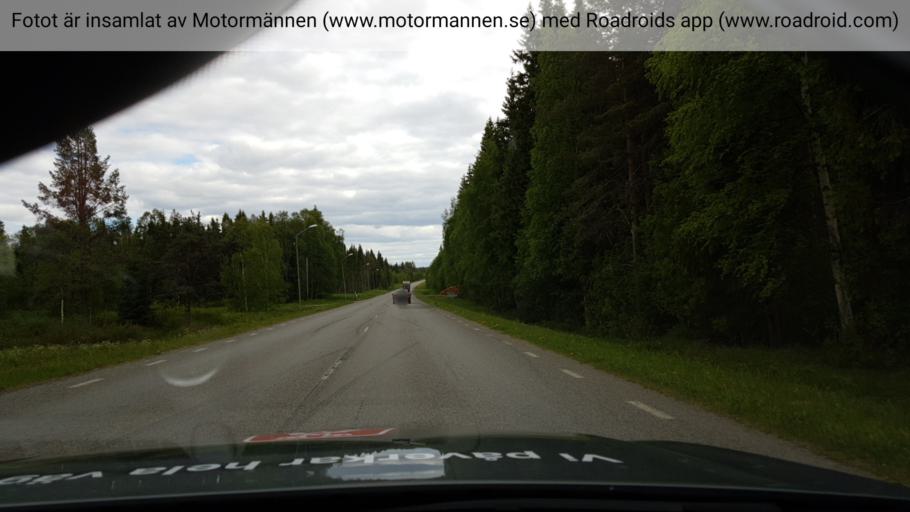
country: SE
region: Jaemtland
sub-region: Stroemsunds Kommun
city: Stroemsund
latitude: 63.8893
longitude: 15.5417
